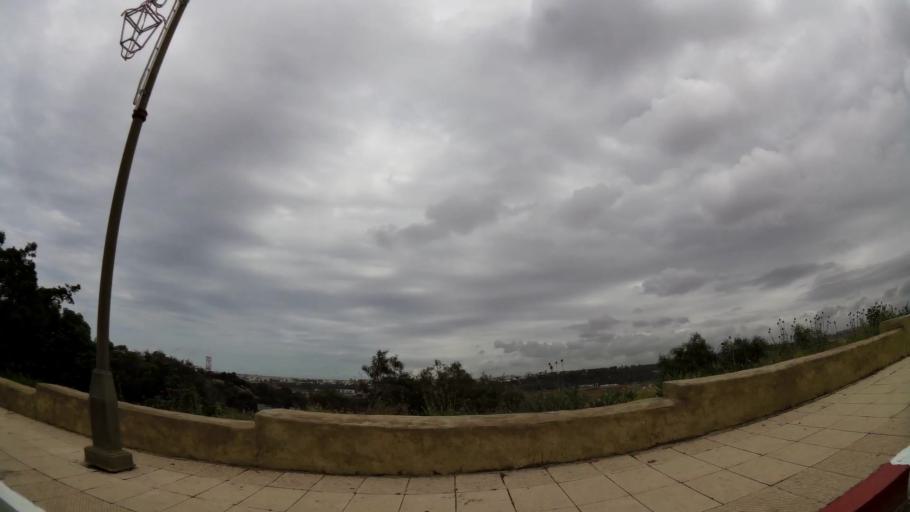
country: MA
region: Rabat-Sale-Zemmour-Zaer
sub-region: Rabat
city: Rabat
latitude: 34.0159
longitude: -6.8207
